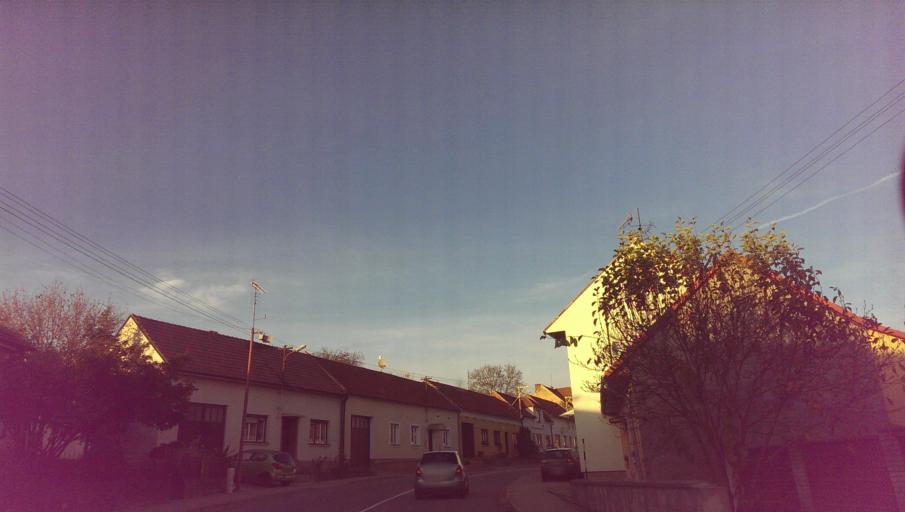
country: CZ
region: Zlin
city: Brezolupy
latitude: 49.1237
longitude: 17.5857
